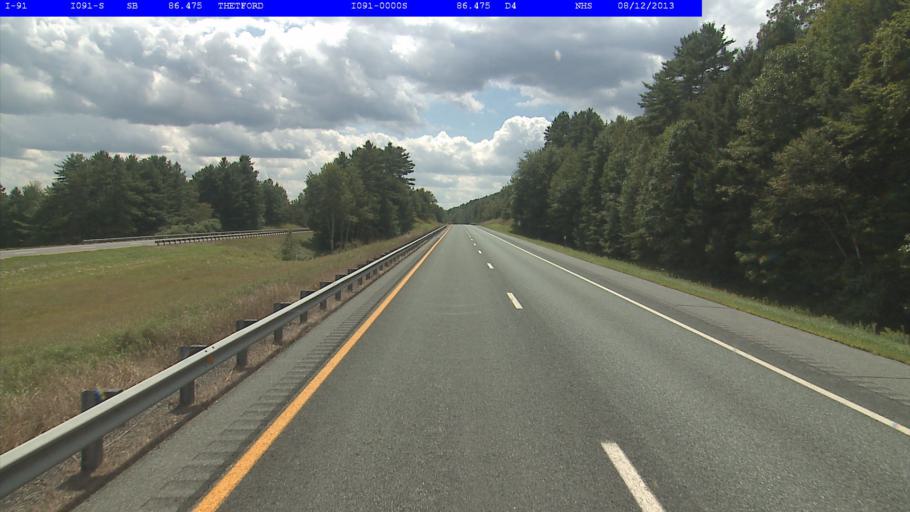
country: US
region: New Hampshire
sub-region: Grafton County
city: Lyme
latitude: 43.8433
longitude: -72.2007
